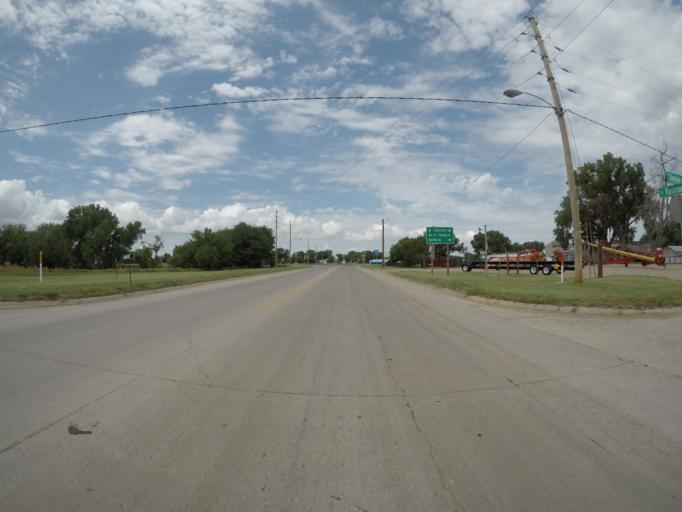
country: US
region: Kansas
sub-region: Rawlins County
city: Atwood
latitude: 39.8121
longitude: -101.0468
